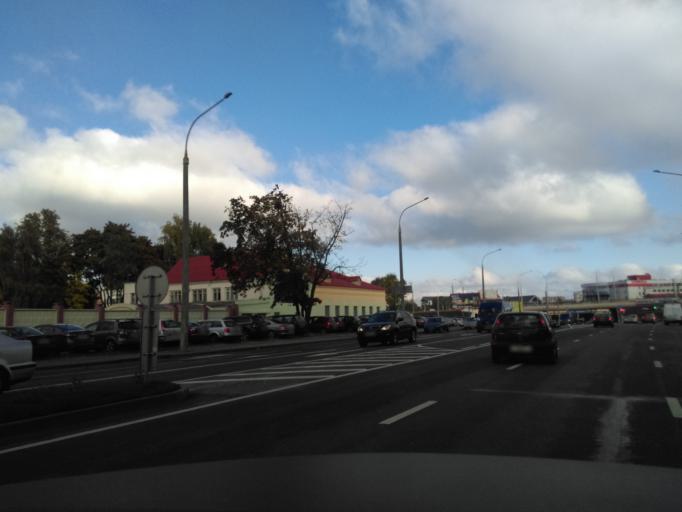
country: BY
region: Minsk
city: Minsk
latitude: 53.8852
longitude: 27.5795
